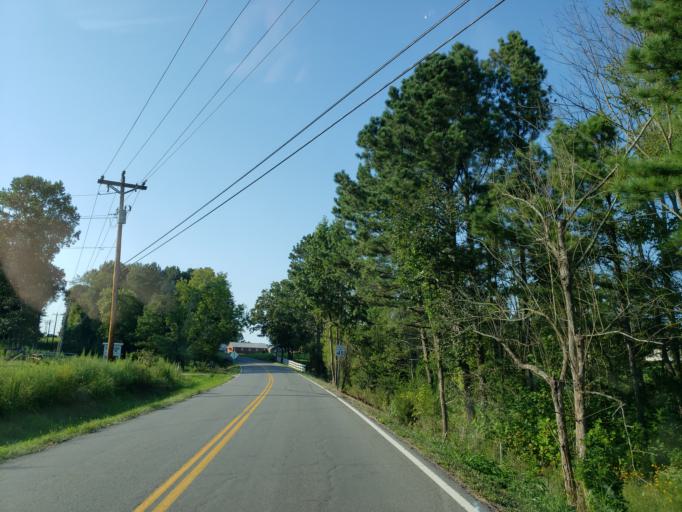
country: US
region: Tennessee
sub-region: Bradley County
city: Wildwood Lake
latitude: 35.0642
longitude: -84.7660
